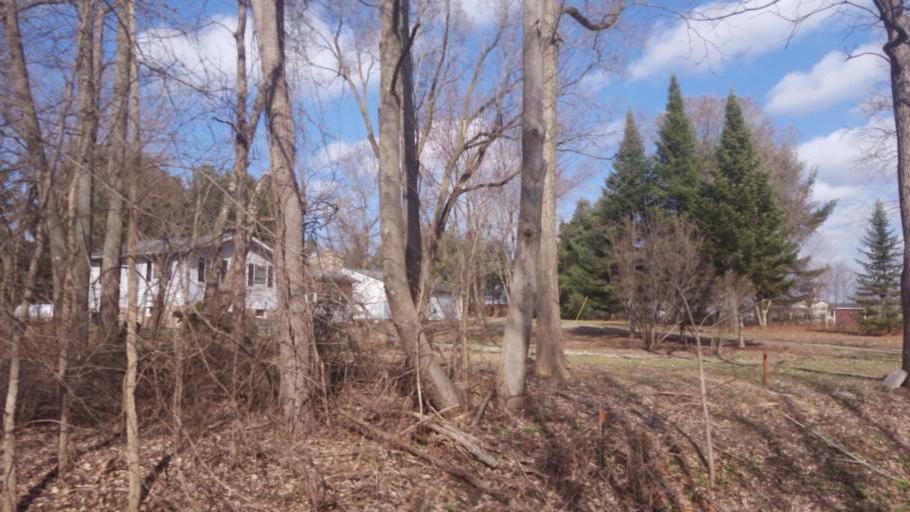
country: US
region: Ohio
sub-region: Knox County
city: Centerburg
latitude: 40.4226
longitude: -82.6529
